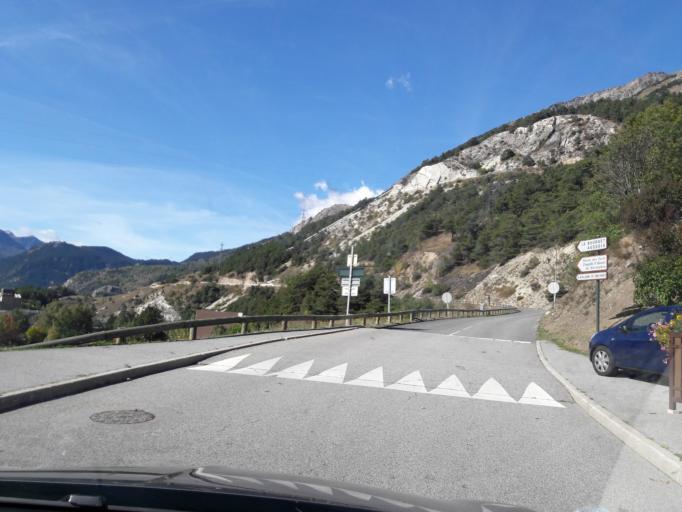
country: FR
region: Rhone-Alpes
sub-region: Departement de la Savoie
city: Modane
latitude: 45.2160
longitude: 6.7194
